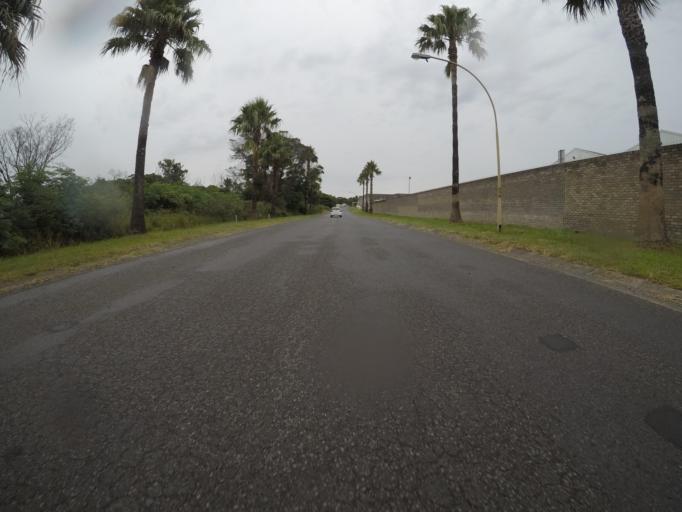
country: ZA
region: Eastern Cape
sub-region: Buffalo City Metropolitan Municipality
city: East London
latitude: -32.9717
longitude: 27.8186
